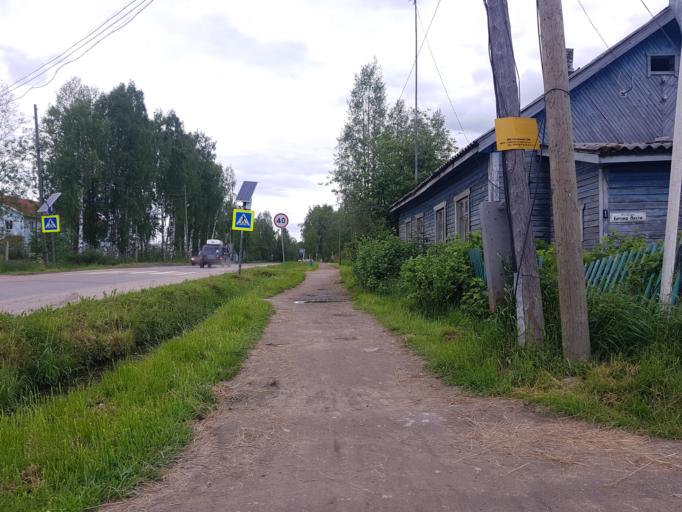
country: RU
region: Republic of Karelia
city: Kalevala
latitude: 65.2017
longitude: 31.1762
